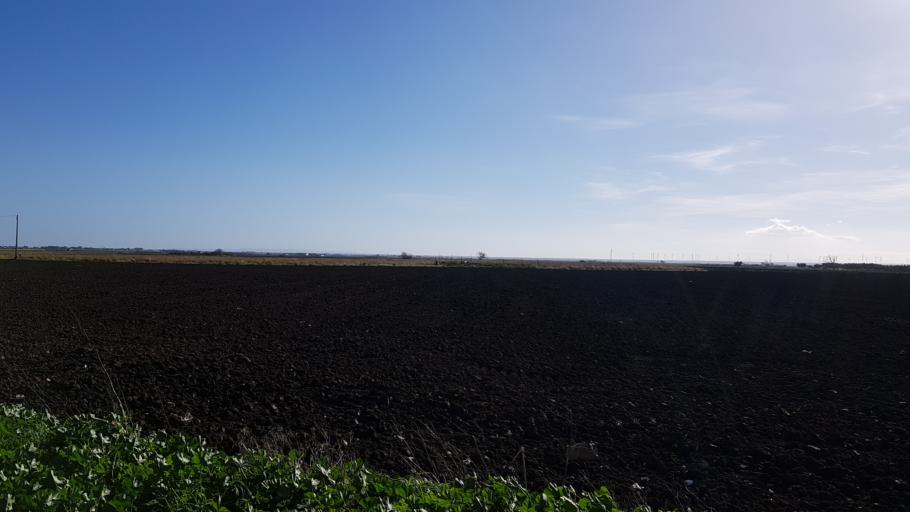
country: IT
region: Apulia
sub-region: Provincia di Foggia
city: Carapelle
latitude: 41.3823
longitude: 15.6462
